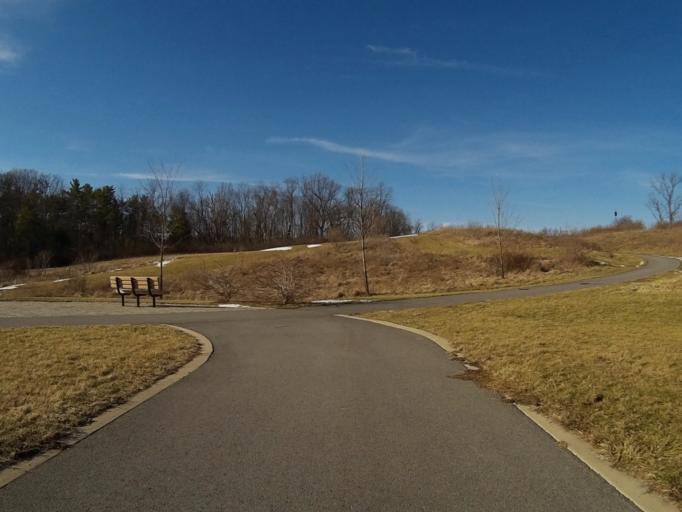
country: US
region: Pennsylvania
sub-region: Centre County
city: Houserville
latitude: 40.8497
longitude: -77.8777
